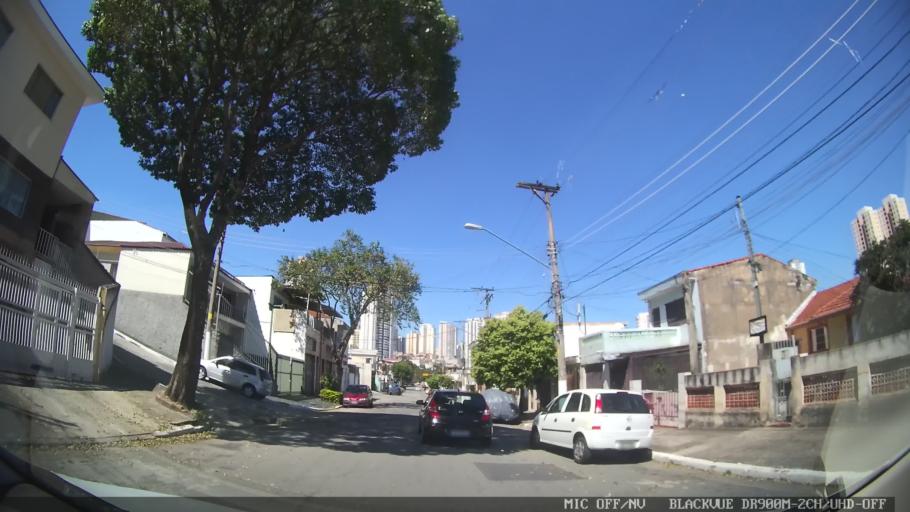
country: BR
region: Sao Paulo
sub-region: Sao Paulo
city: Sao Paulo
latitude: -23.4954
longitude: -46.6485
